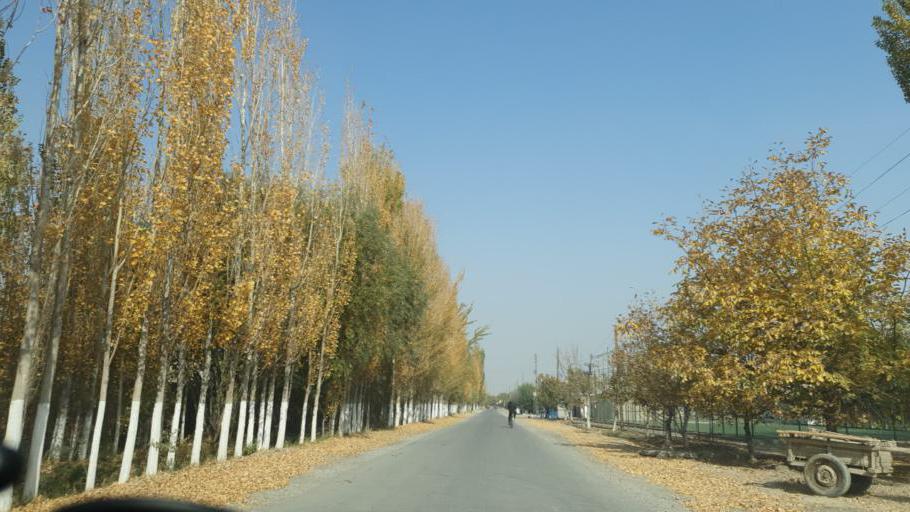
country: UZ
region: Fergana
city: Beshariq
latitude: 40.4912
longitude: 70.6208
